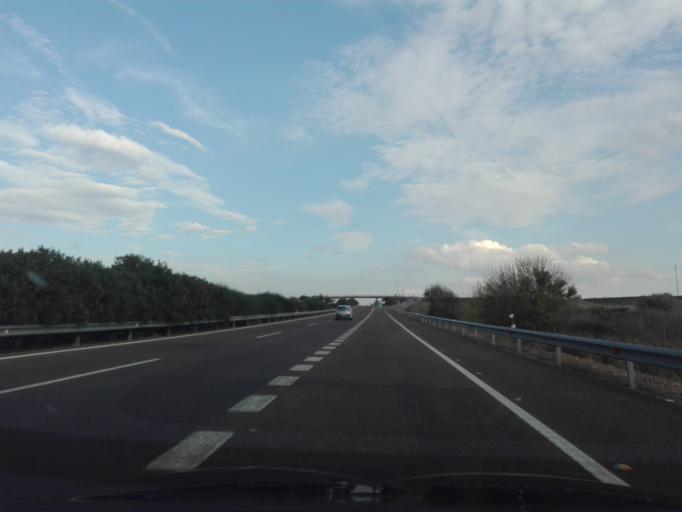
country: ES
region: Extremadura
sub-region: Provincia de Badajoz
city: Valdelacalzada
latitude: 38.8514
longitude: -6.7185
